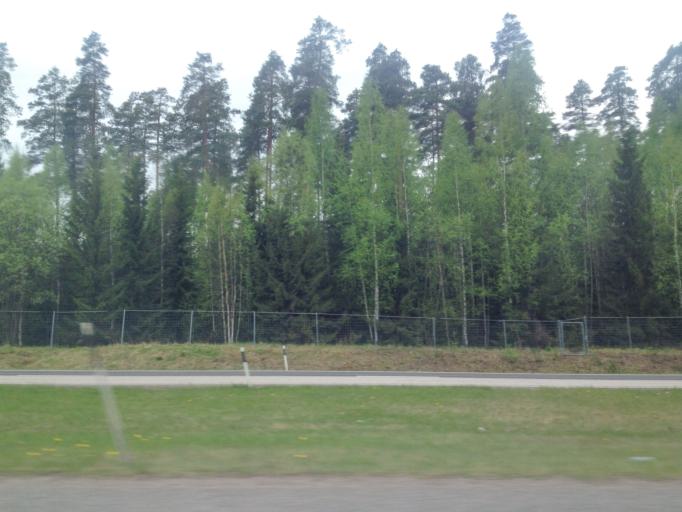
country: FI
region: Uusimaa
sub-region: Helsinki
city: Nurmijaervi
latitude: 60.4755
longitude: 24.8495
